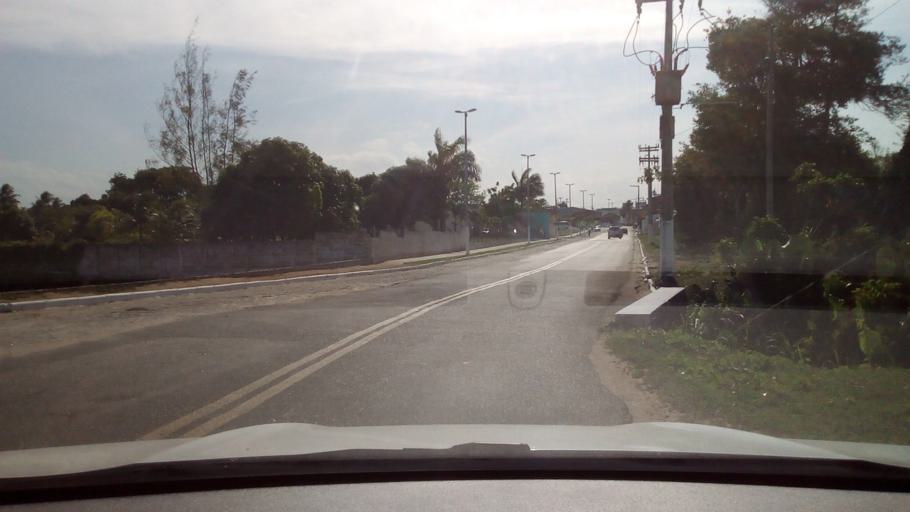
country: BR
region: Rio Grande do Norte
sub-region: Goianinha
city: Goianinha
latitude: -6.2654
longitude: -35.2033
